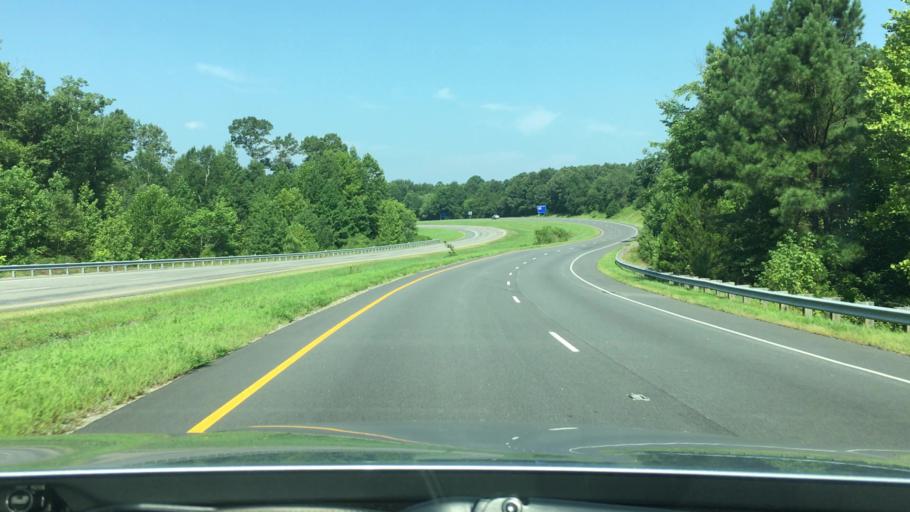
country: US
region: Virginia
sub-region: Caroline County
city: Bowling Green
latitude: 38.0378
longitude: -77.3548
